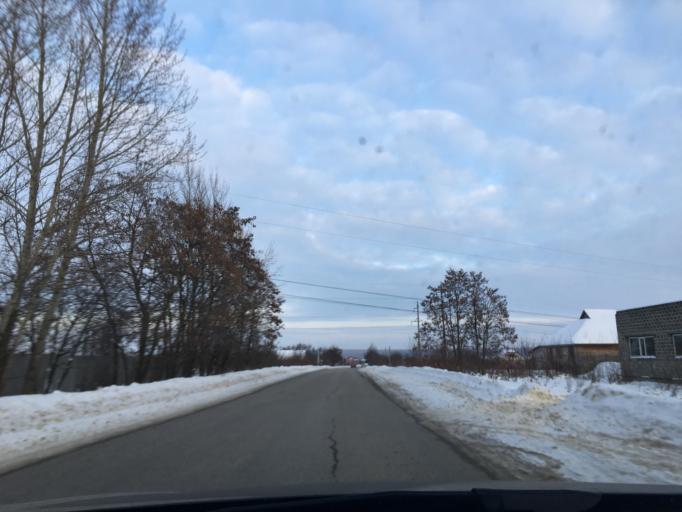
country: RU
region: Belgorod
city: Severnyy
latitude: 50.6978
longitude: 36.5762
